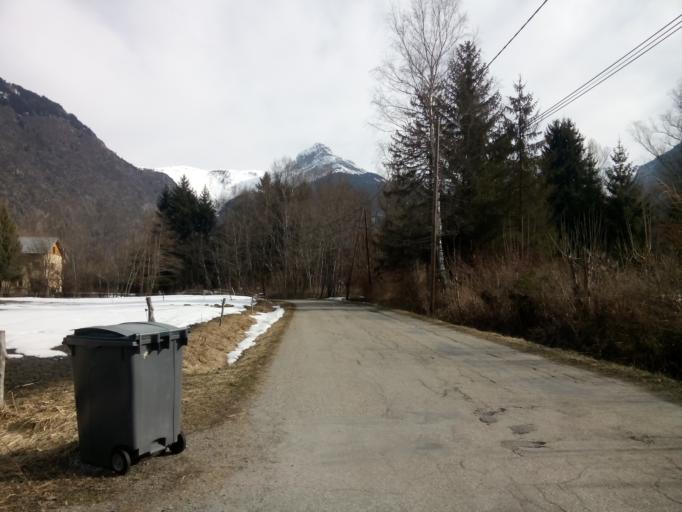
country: FR
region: Rhone-Alpes
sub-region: Departement de l'Isere
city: Huez
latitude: 45.0472
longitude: 6.0446
